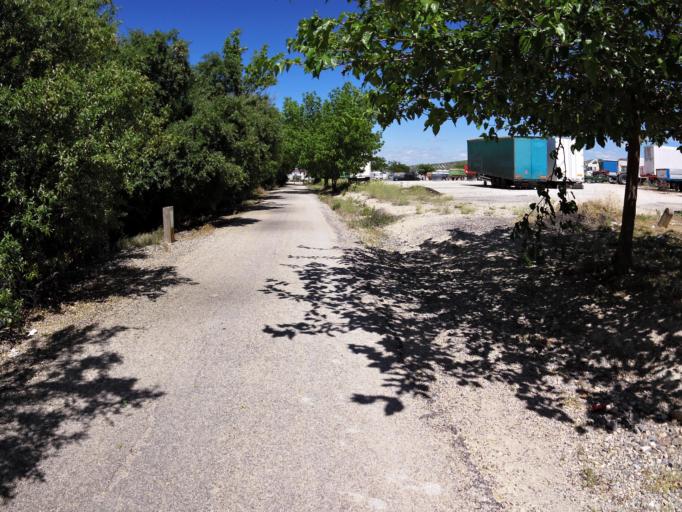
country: ES
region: Andalusia
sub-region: Provincia de Jaen
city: Torre del Campo
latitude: 37.7781
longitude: -3.8976
